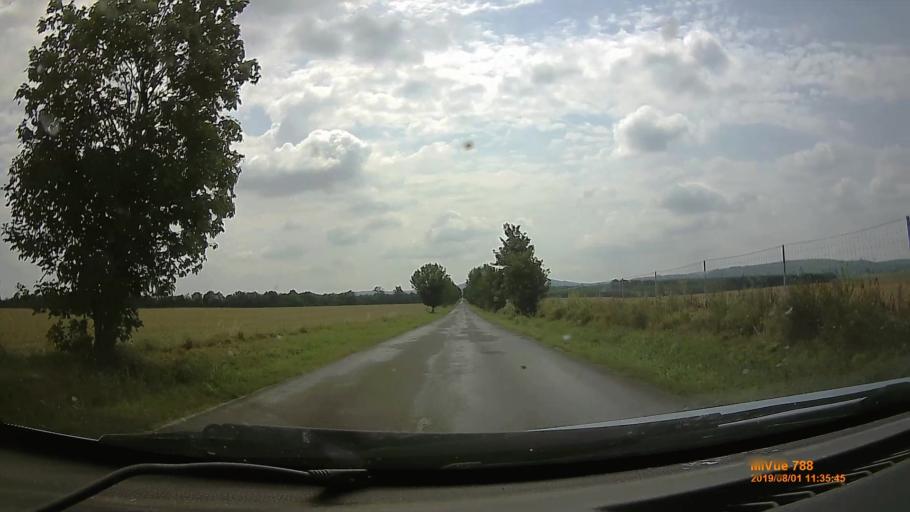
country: HU
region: Baranya
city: Villany
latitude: 45.9242
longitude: 18.3702
